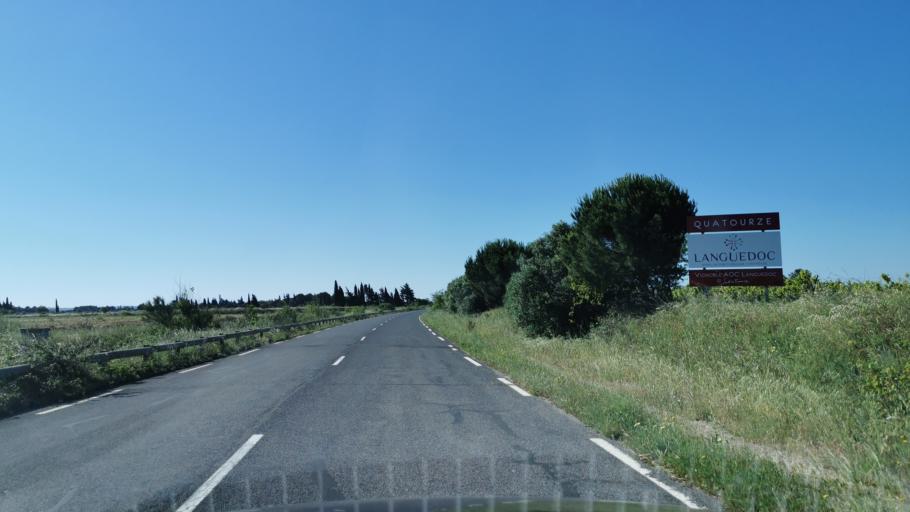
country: FR
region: Languedoc-Roussillon
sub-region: Departement de l'Aude
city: Narbonne
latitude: 43.1559
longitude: 2.9962
